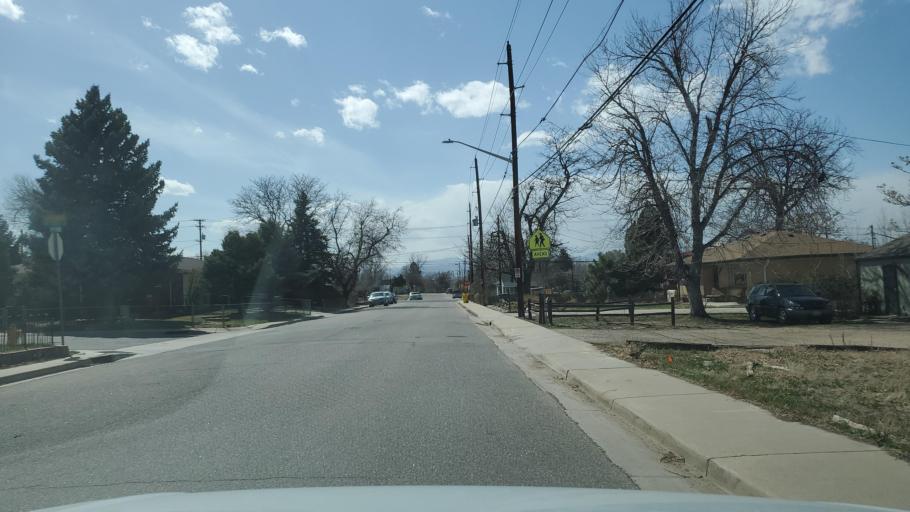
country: US
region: Colorado
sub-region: Adams County
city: Berkley
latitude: 39.7948
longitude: -105.0333
